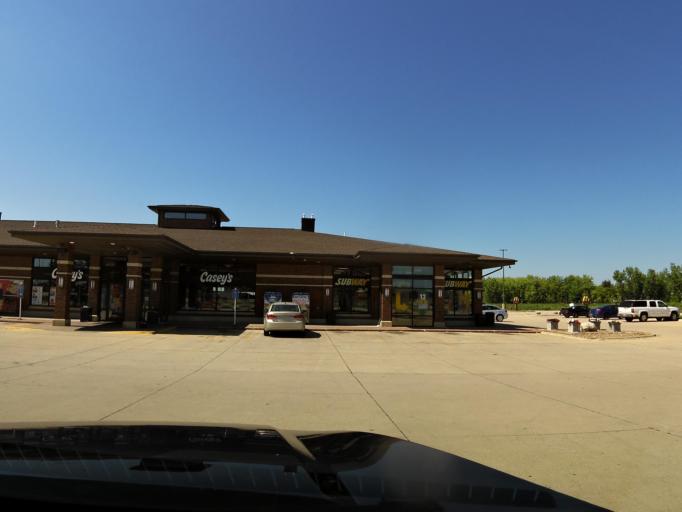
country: US
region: Iowa
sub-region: Linn County
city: Center Point
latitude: 42.1729
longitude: -91.7770
